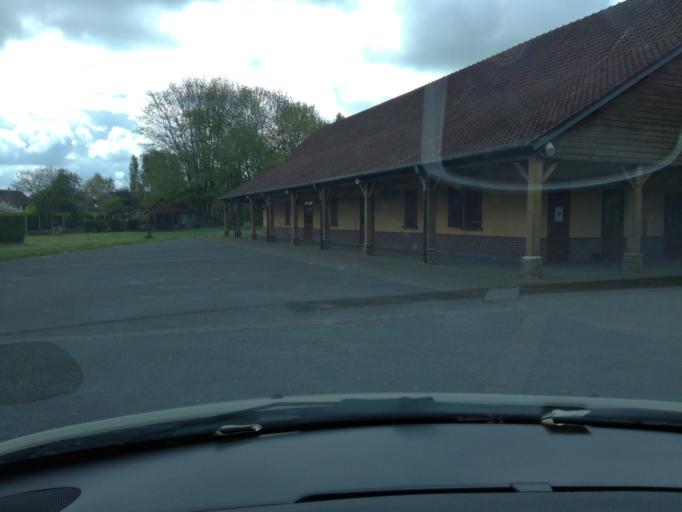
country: FR
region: Picardie
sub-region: Departement de la Somme
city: Pont-Remy
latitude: 50.0637
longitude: 1.8830
